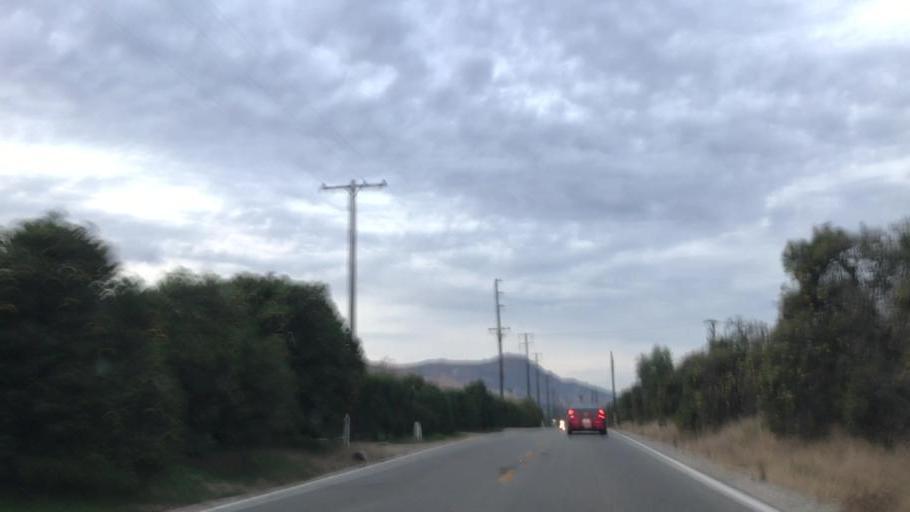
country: US
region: California
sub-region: Ventura County
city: Fillmore
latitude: 34.3635
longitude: -118.9455
